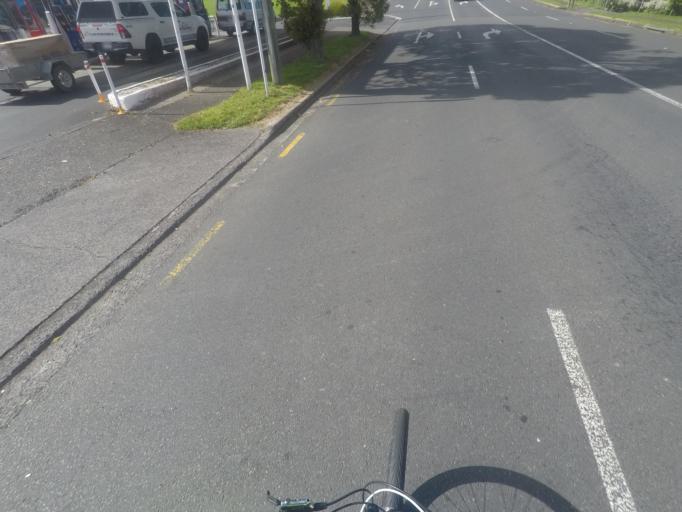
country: NZ
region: Auckland
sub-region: Auckland
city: Mangere
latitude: -36.9259
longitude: 174.7836
